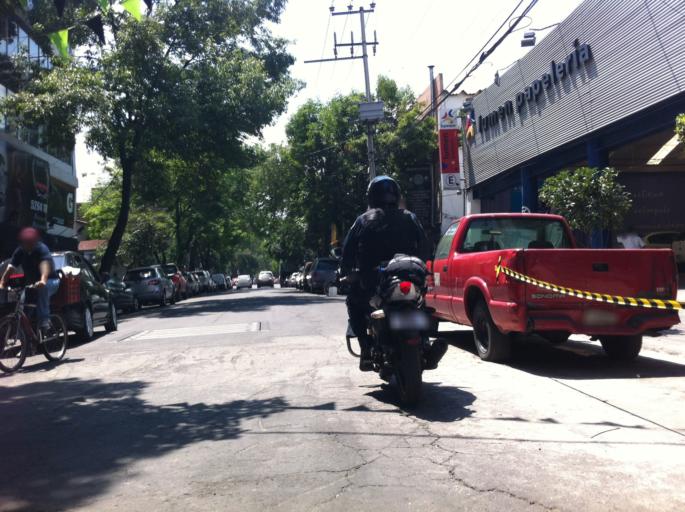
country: MX
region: Mexico City
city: Benito Juarez
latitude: 19.4113
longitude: -99.1629
